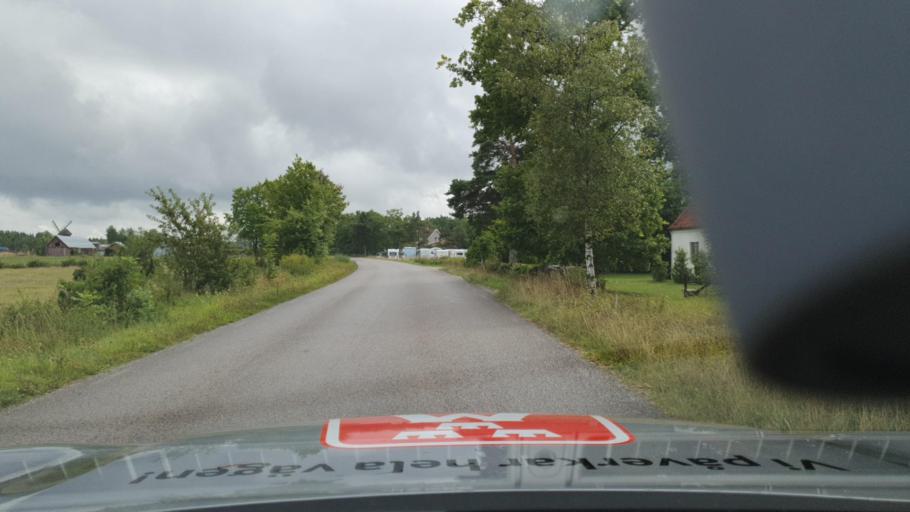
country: SE
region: Gotland
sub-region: Gotland
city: Slite
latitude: 57.6856
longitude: 18.7643
